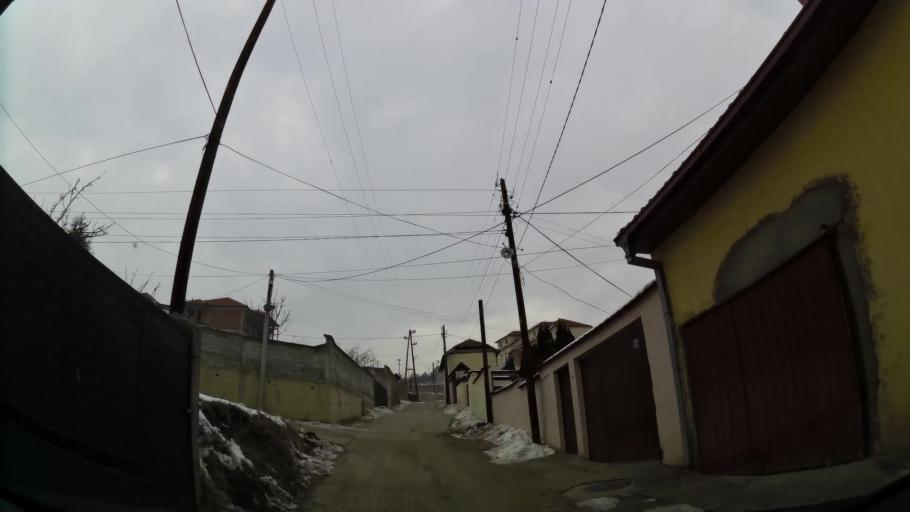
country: MK
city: Kondovo
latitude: 42.0134
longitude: 21.3142
